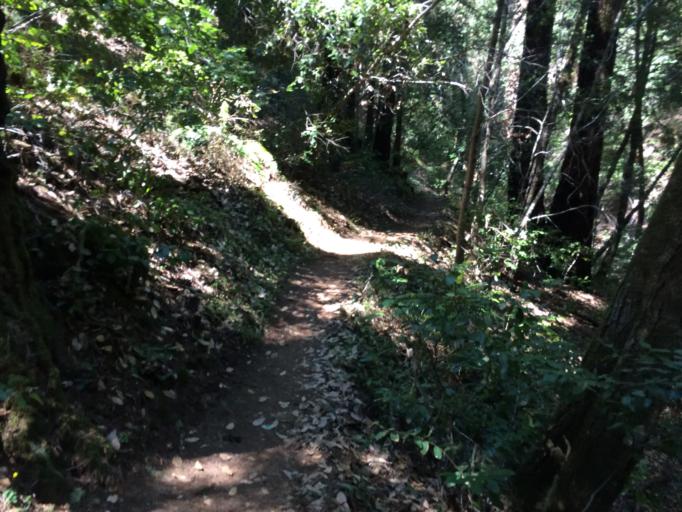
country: US
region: California
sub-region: Santa Cruz County
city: Boulder Creek
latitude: 37.1940
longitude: -122.2230
